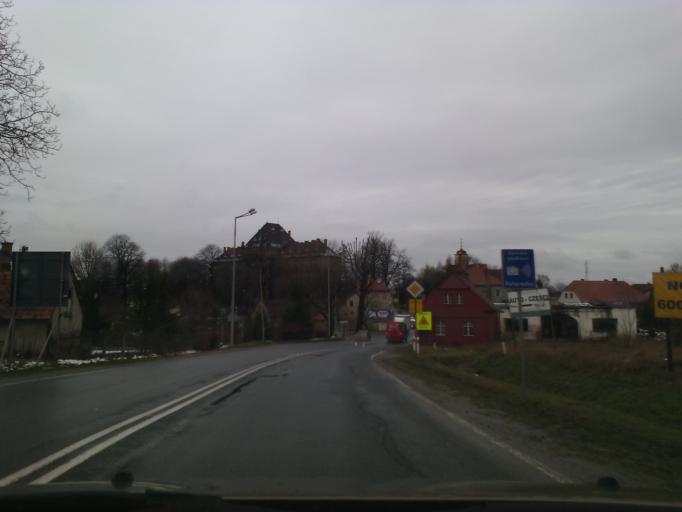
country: PL
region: Lower Silesian Voivodeship
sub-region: Powiat swidnicki
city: Swiebodzice
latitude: 50.8503
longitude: 16.3724
